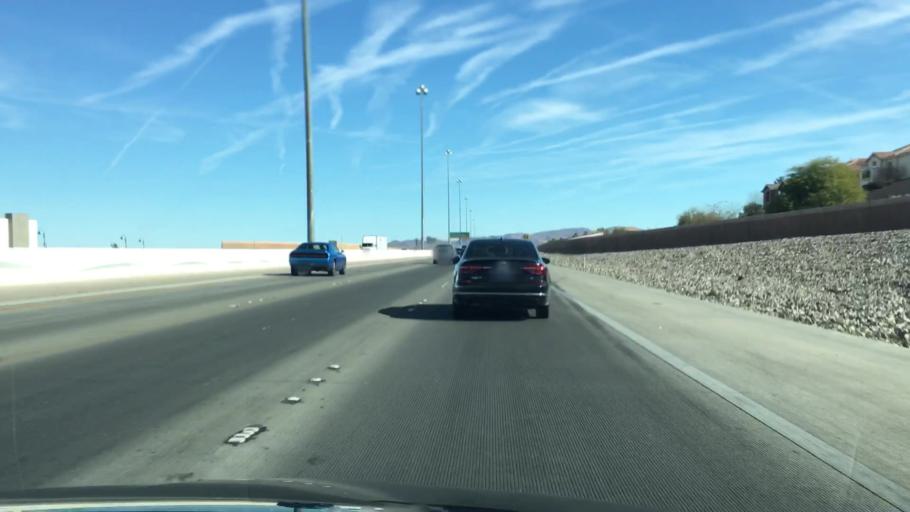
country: US
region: Nevada
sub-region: Clark County
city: Whitney
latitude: 36.0295
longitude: -115.0453
